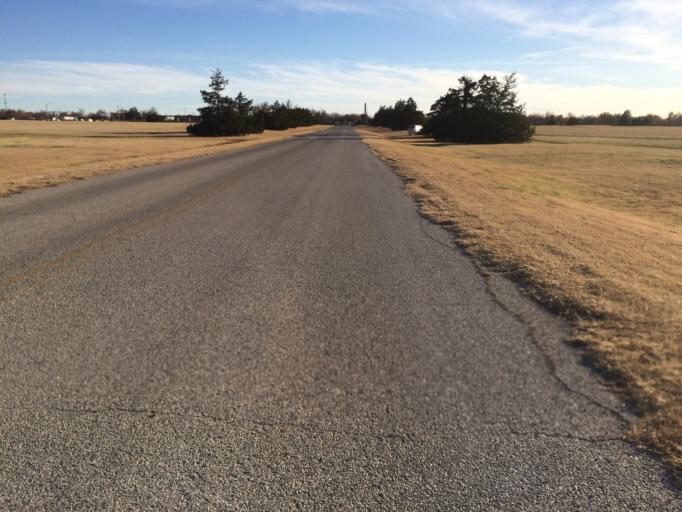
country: US
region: Oklahoma
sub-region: Cleveland County
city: Norman
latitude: 35.2367
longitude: -97.4553
